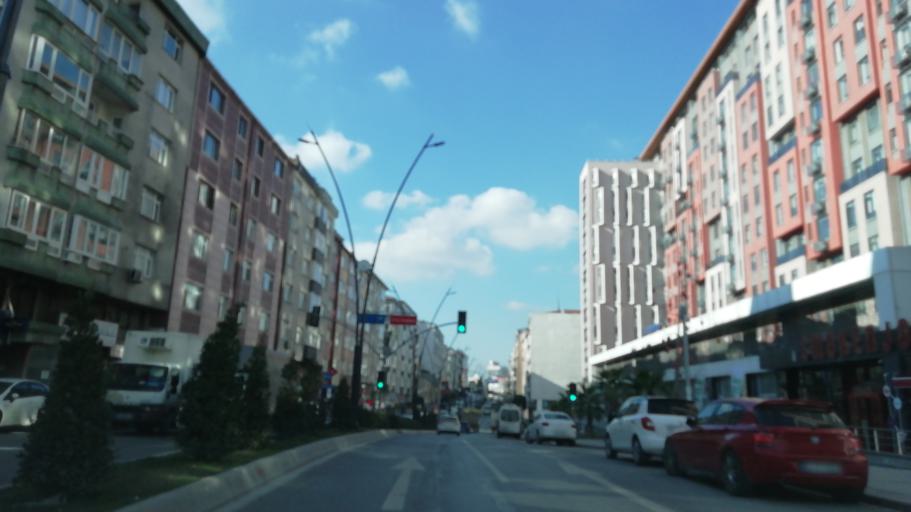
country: TR
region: Istanbul
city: Esenler
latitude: 41.0579
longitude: 28.9216
